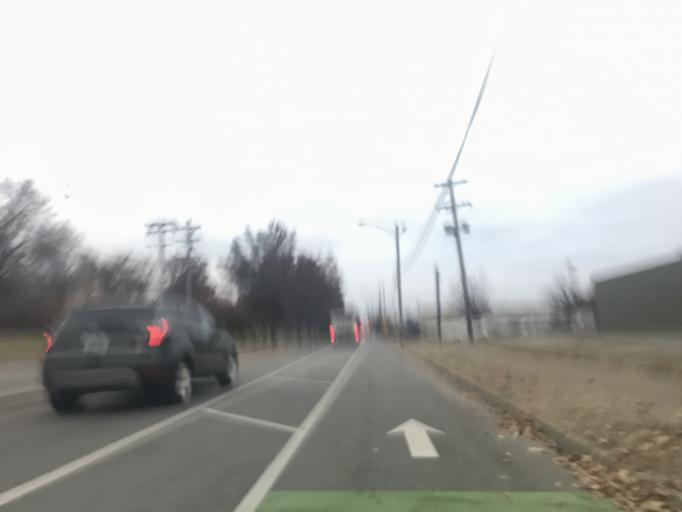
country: US
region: Kentucky
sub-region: Jefferson County
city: Louisville
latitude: 38.2527
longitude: -85.7726
